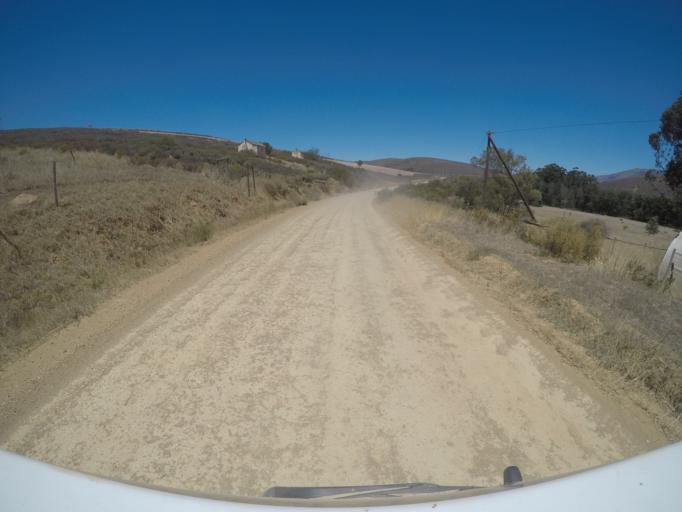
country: ZA
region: Western Cape
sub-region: Overberg District Municipality
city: Caledon
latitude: -34.1387
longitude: 19.2480
